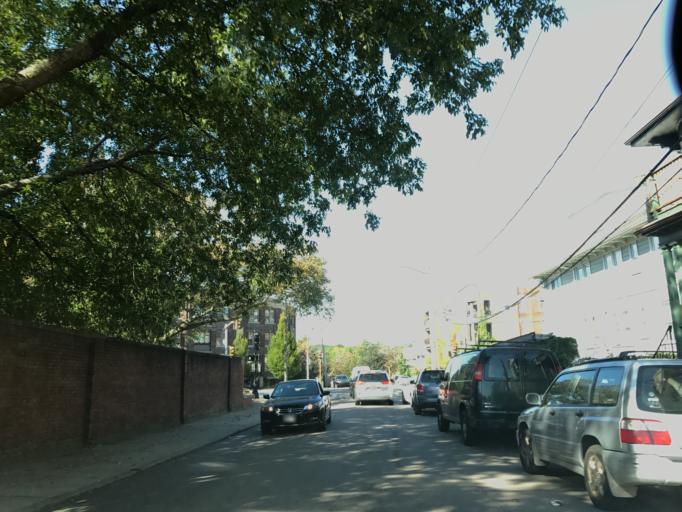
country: US
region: Massachusetts
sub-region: Norfolk County
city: Brookline
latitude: 42.3238
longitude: -71.1116
